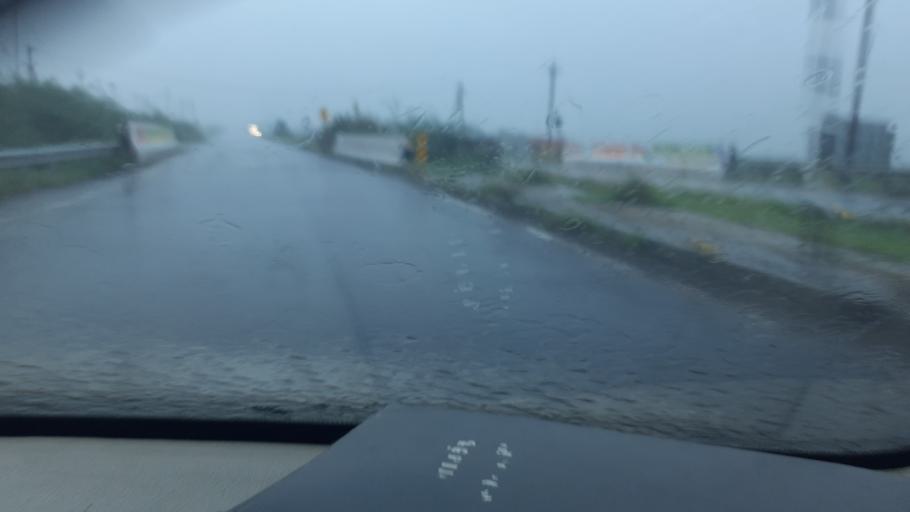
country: IN
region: Tamil Nadu
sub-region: Virudhunagar
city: Sattur
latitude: 9.4354
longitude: 77.9204
